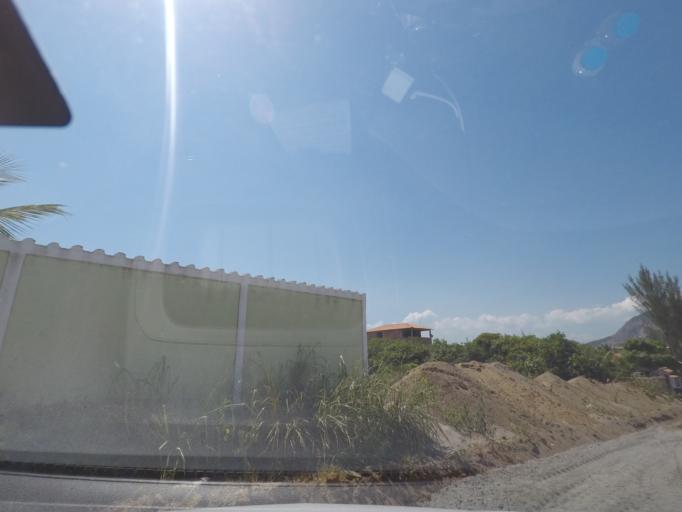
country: BR
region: Rio de Janeiro
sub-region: Marica
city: Marica
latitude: -22.9715
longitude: -42.9073
